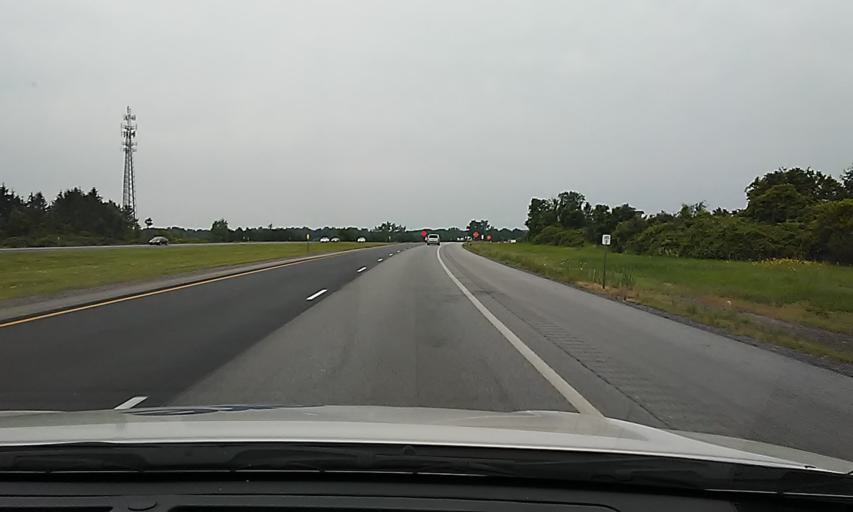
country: US
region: New York
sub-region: Genesee County
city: Batavia
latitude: 43.0148
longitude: -78.0935
